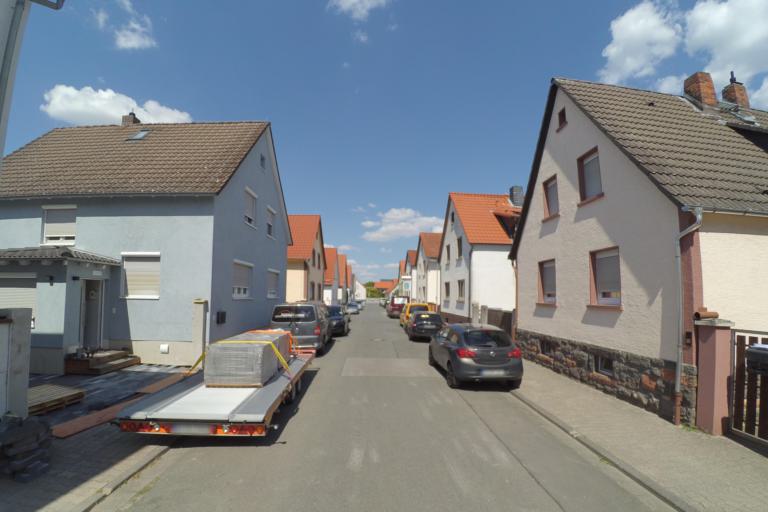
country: DE
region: Hesse
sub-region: Regierungsbezirk Darmstadt
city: Alsbach-Hahnlein
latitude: 49.7388
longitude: 8.5720
